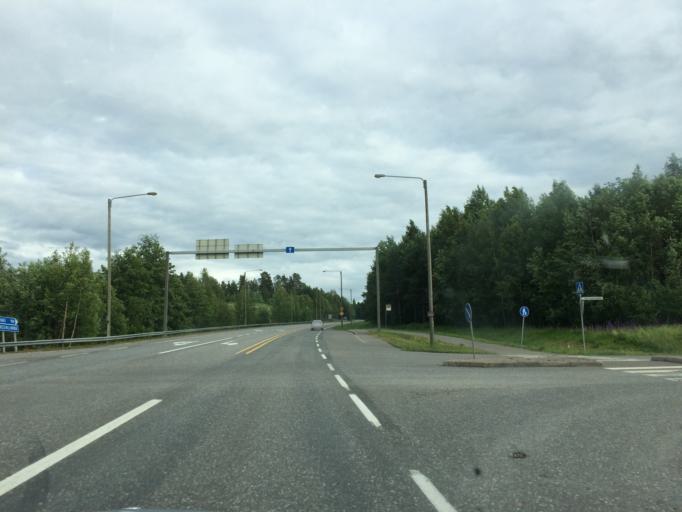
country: FI
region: Haeme
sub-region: Haemeenlinna
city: Haemeenlinna
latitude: 60.9661
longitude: 24.4799
